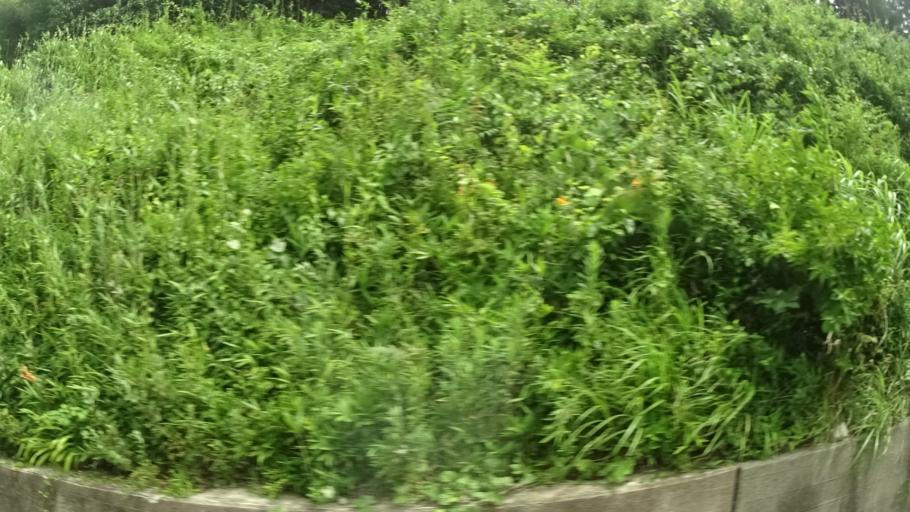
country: JP
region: Fukushima
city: Namie
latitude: 37.3304
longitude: 141.0232
